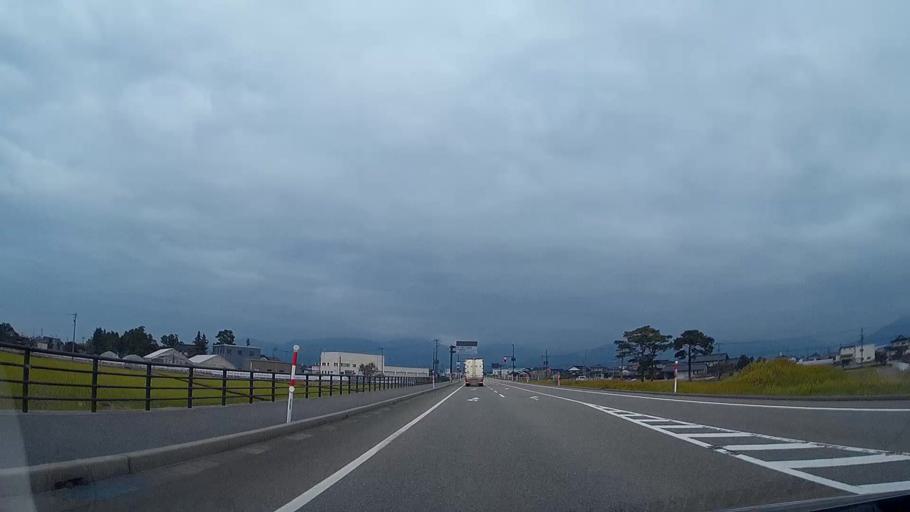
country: JP
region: Toyama
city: Nyuzen
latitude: 36.9271
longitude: 137.4858
